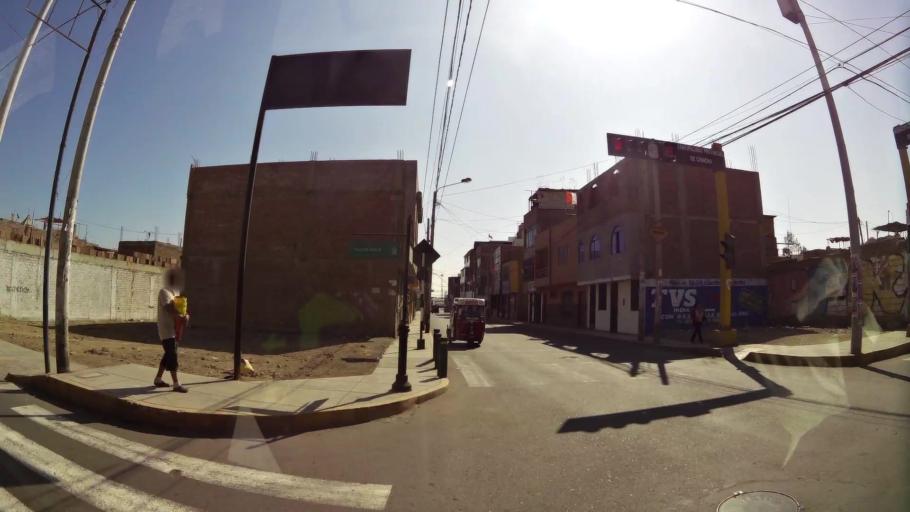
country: PE
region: Ica
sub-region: Provincia de Chincha
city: Chincha Alta
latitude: -13.4152
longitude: -76.1313
